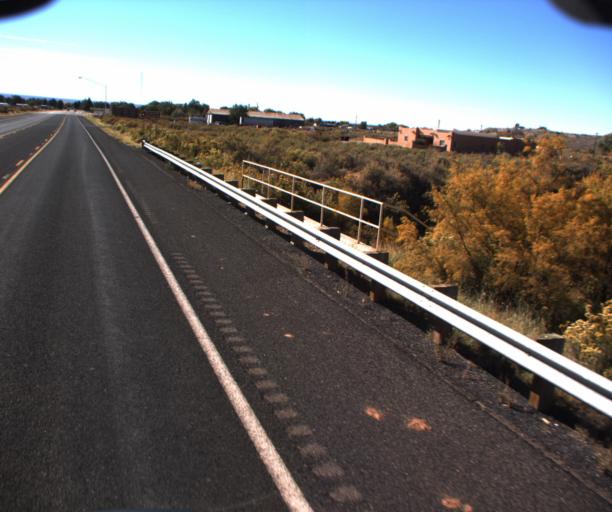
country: US
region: Arizona
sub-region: Coconino County
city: Fredonia
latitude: 36.9637
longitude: -112.5270
